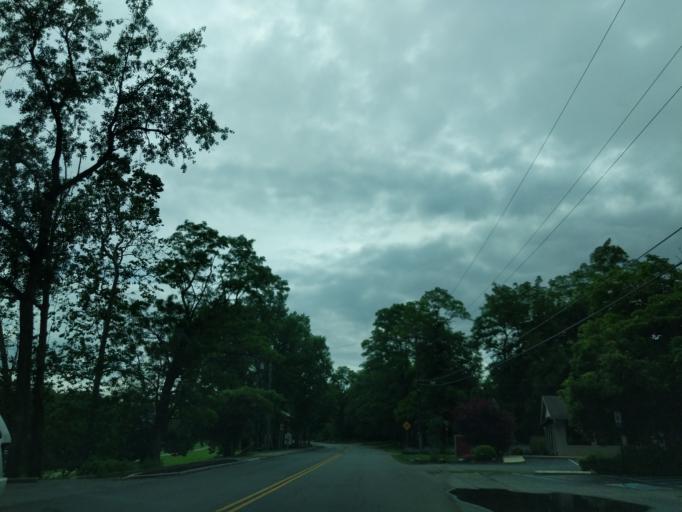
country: US
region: Indiana
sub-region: Delaware County
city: Muncie
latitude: 40.1918
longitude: -85.4039
